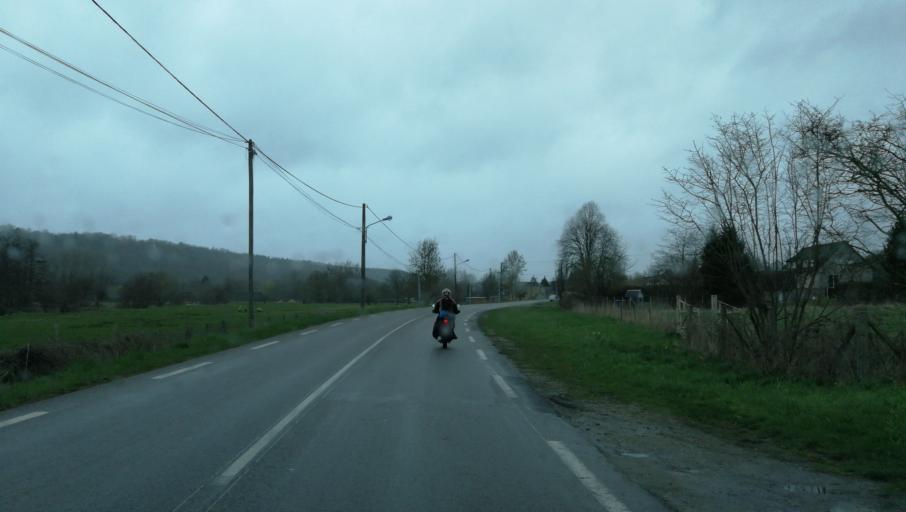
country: FR
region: Haute-Normandie
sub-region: Departement de l'Eure
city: Brionne
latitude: 49.1643
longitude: 0.7248
